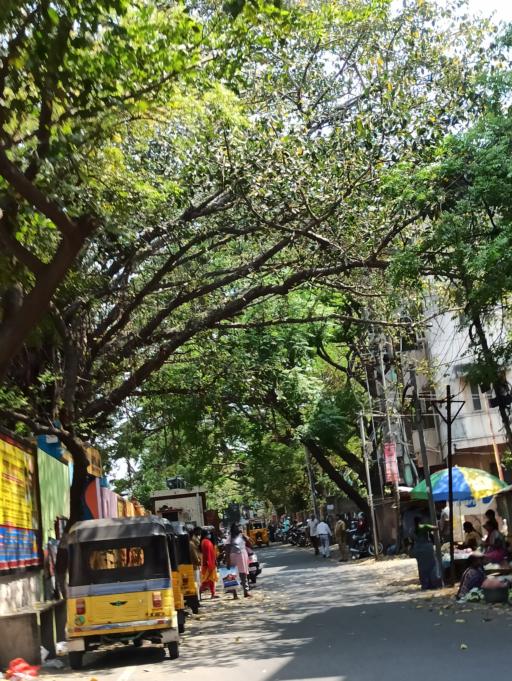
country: IN
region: Tamil Nadu
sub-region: Chennai
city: Chetput
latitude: 13.0658
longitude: 80.2325
